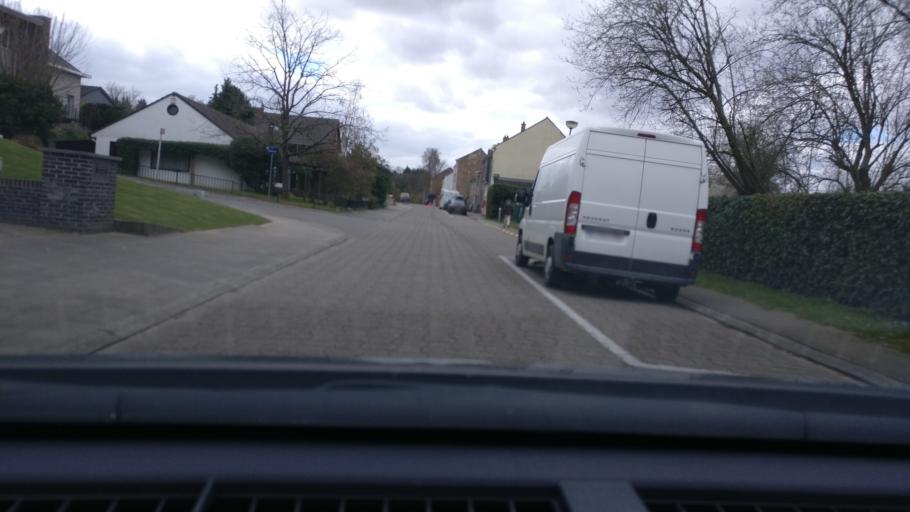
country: BE
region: Flanders
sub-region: Provincie Vlaams-Brabant
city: Tervuren
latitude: 50.8192
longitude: 4.5137
